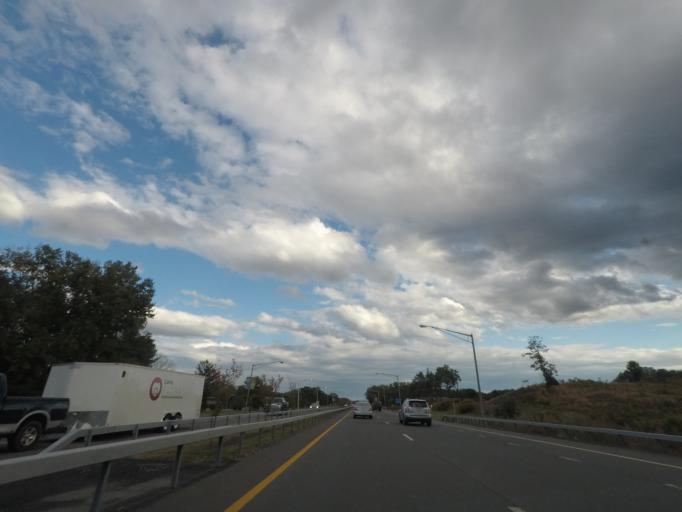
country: US
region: New York
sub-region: Albany County
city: Westmere
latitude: 42.7116
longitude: -73.8698
